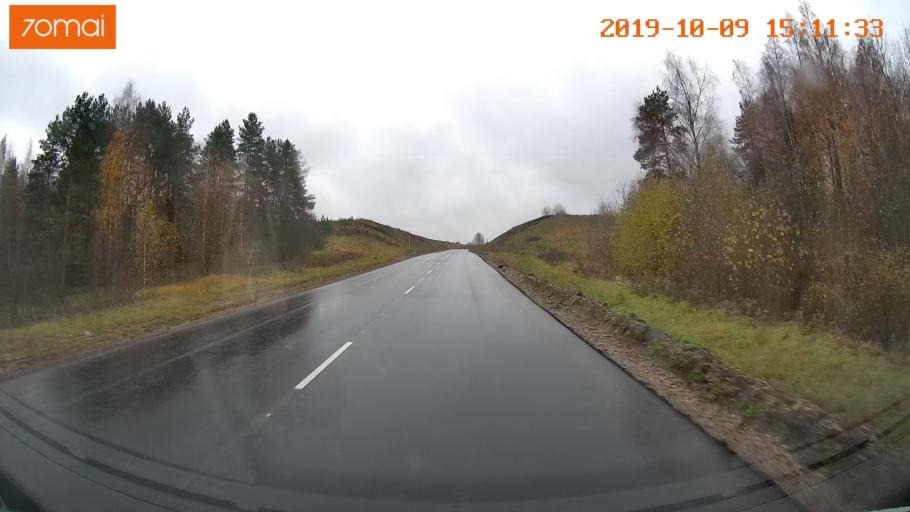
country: RU
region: Kostroma
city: Susanino
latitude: 58.1634
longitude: 41.6294
